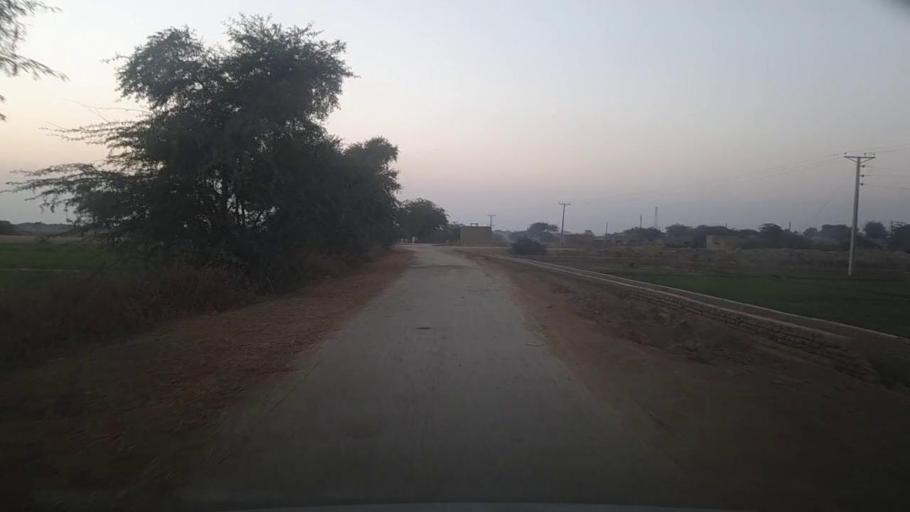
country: PK
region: Sindh
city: Khairpur Nathan Shah
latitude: 27.1819
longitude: 67.5997
